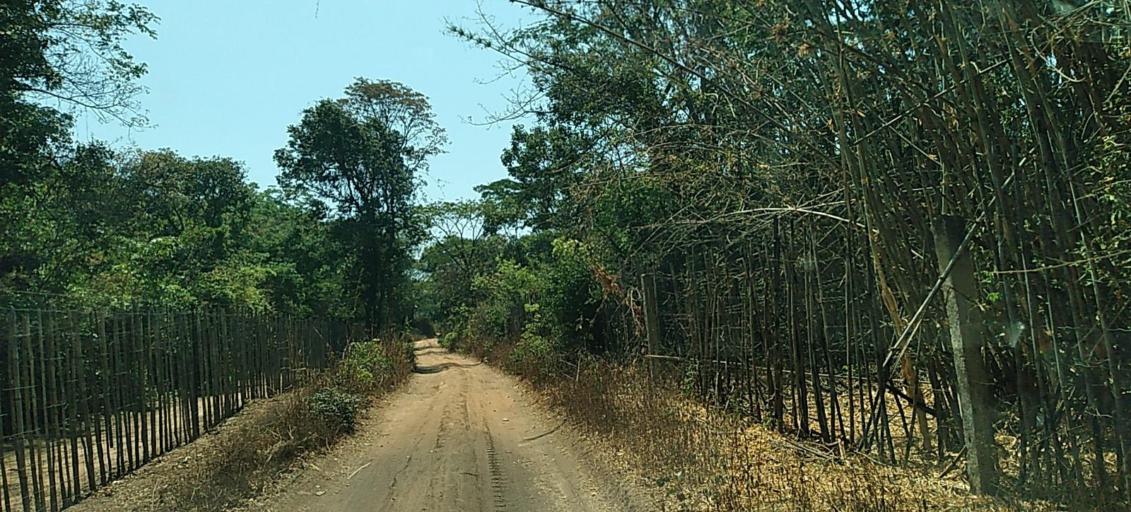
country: ZM
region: Copperbelt
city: Luanshya
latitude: -13.0087
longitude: 28.4564
